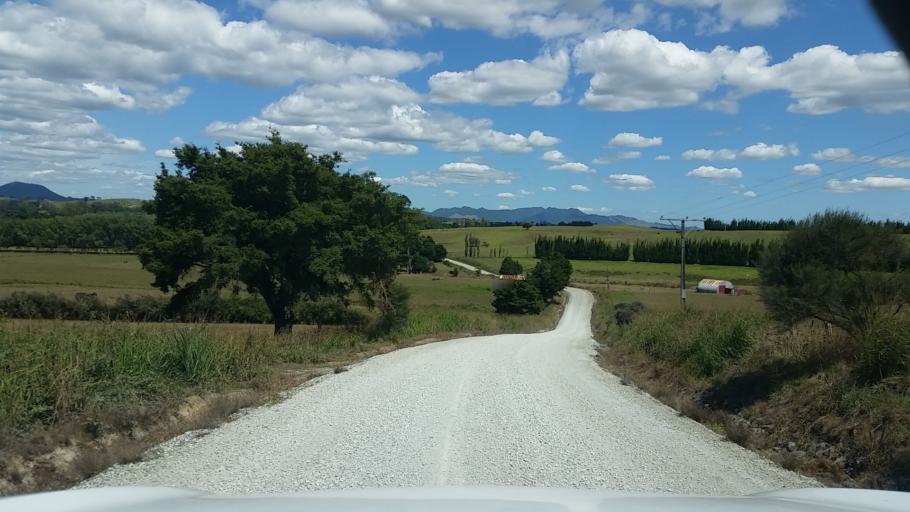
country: NZ
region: Northland
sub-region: Whangarei
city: Maungatapere
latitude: -35.6894
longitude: 174.1445
